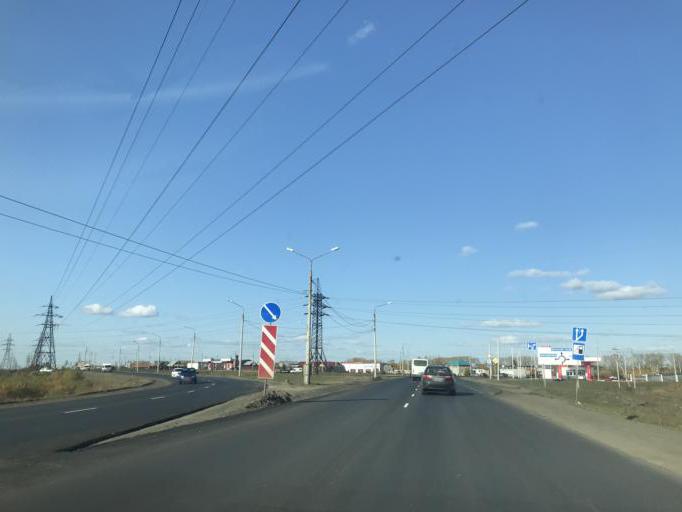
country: RU
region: Chelyabinsk
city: Roshchino
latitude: 55.2285
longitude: 61.2872
